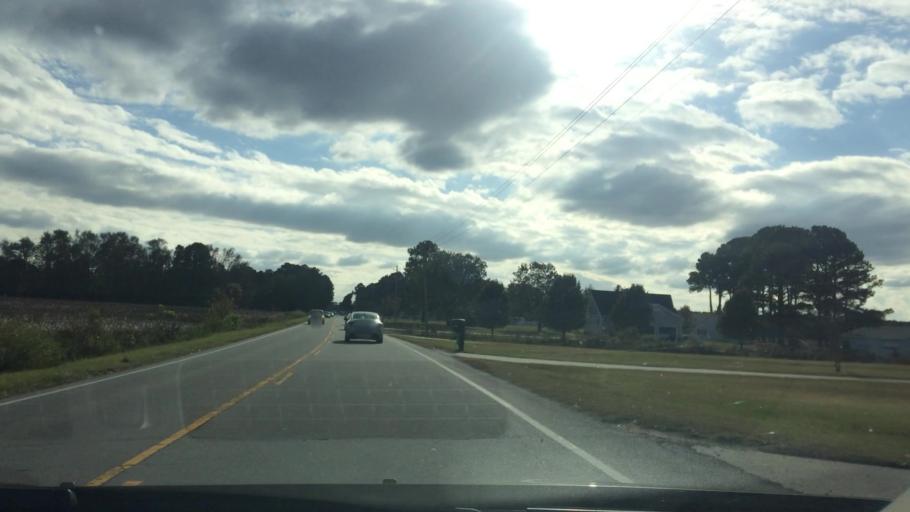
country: US
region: North Carolina
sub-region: Wayne County
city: Elroy
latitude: 35.4248
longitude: -77.8892
